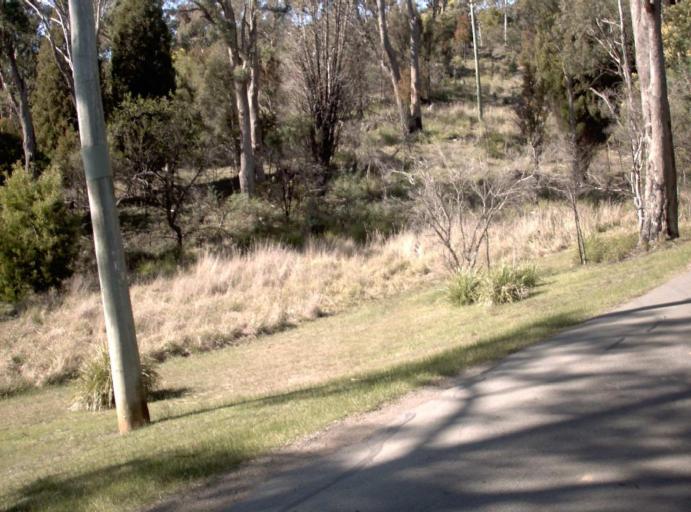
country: AU
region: Tasmania
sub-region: Launceston
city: Newstead
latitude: -41.4563
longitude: 147.1694
